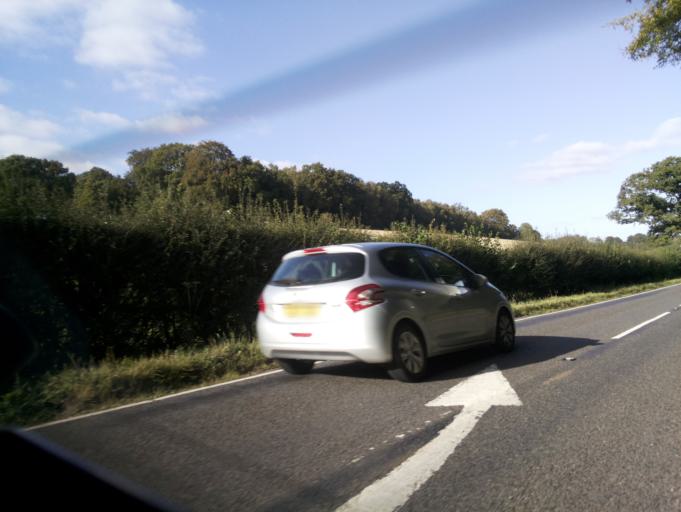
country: GB
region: England
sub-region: Hampshire
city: Four Marks
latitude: 51.0734
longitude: -1.0142
